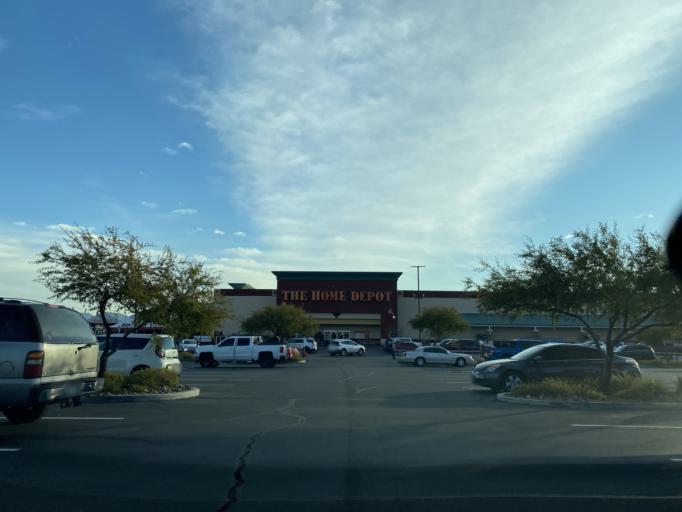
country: US
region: Nevada
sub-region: Clark County
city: Las Vegas
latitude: 36.2705
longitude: -115.2657
